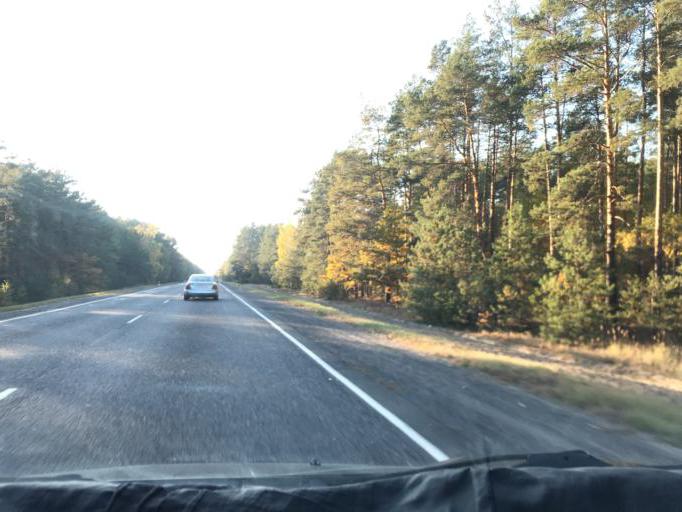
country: BY
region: Gomel
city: Zhytkavichy
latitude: 52.2727
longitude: 28.0566
